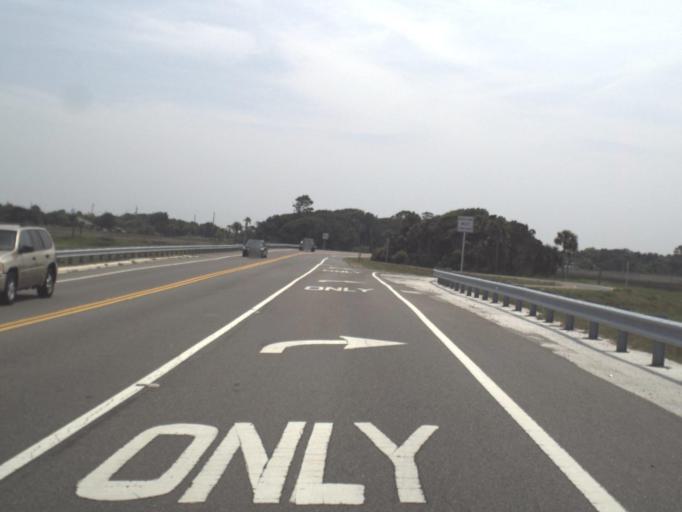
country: US
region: Florida
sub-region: Duval County
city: Atlantic Beach
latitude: 30.4146
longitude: -81.4222
